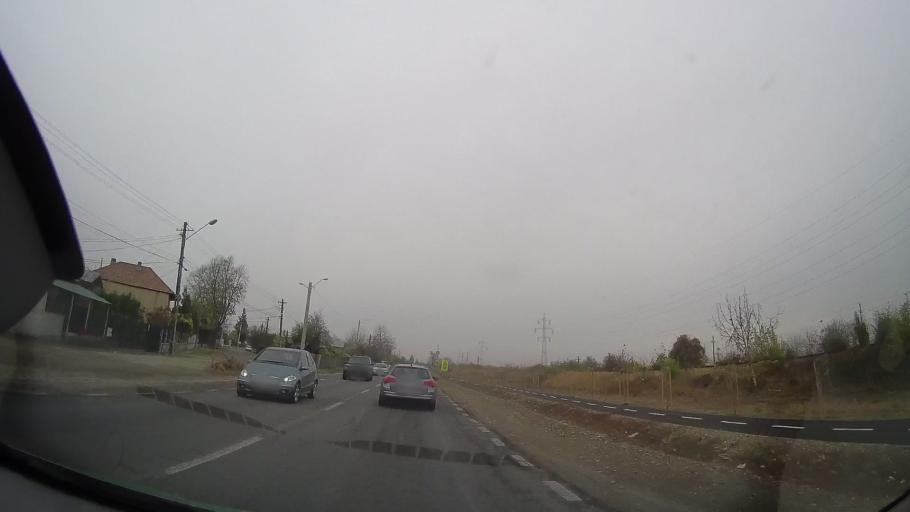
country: RO
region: Prahova
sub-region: Comuna Blejoiu
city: Ploiestiori
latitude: 44.9815
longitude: 26.0163
